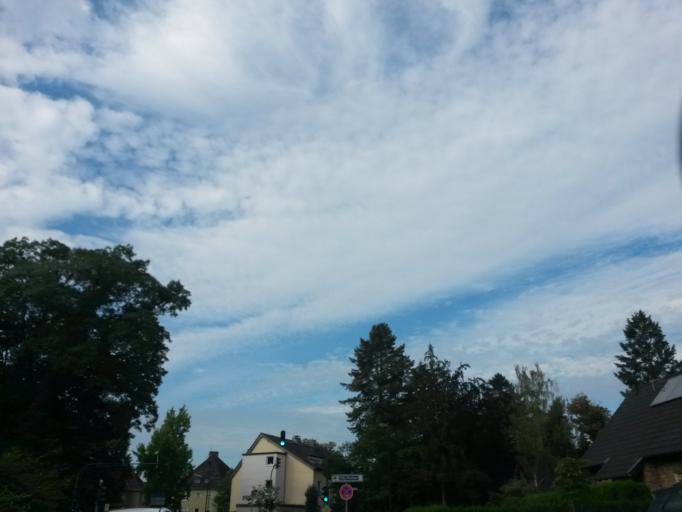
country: DE
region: North Rhine-Westphalia
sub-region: Regierungsbezirk Koln
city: Troisdorf
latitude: 50.8177
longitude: 7.1628
